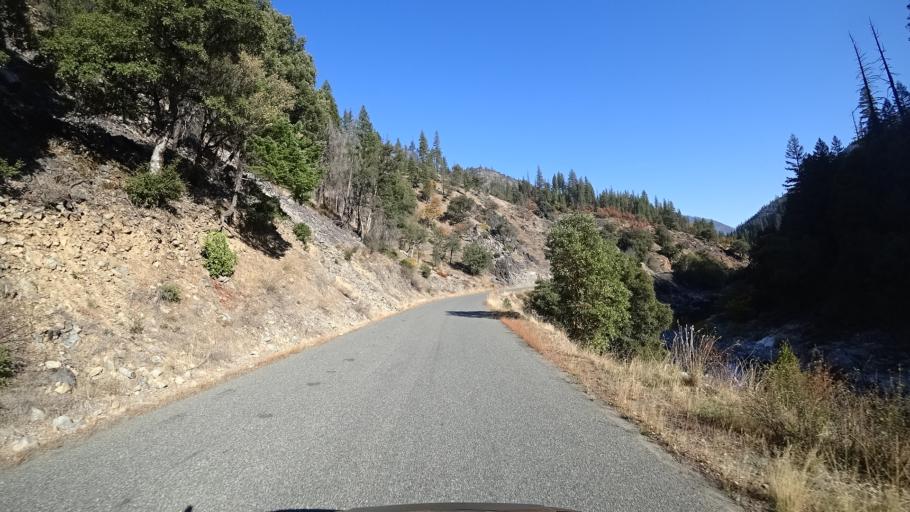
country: US
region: California
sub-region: Siskiyou County
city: Happy Camp
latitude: 41.6632
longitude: -123.1144
